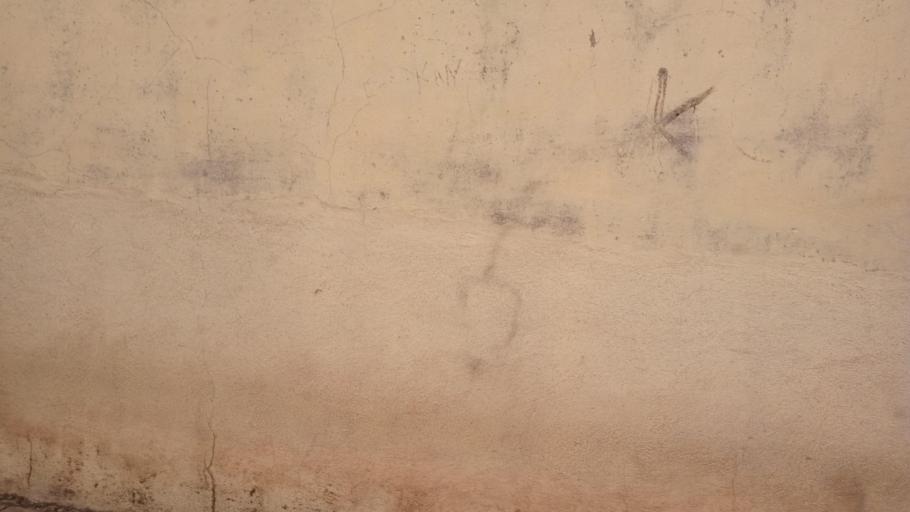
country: GT
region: Quetzaltenango
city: Quetzaltenango
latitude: 14.8302
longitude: -91.5242
